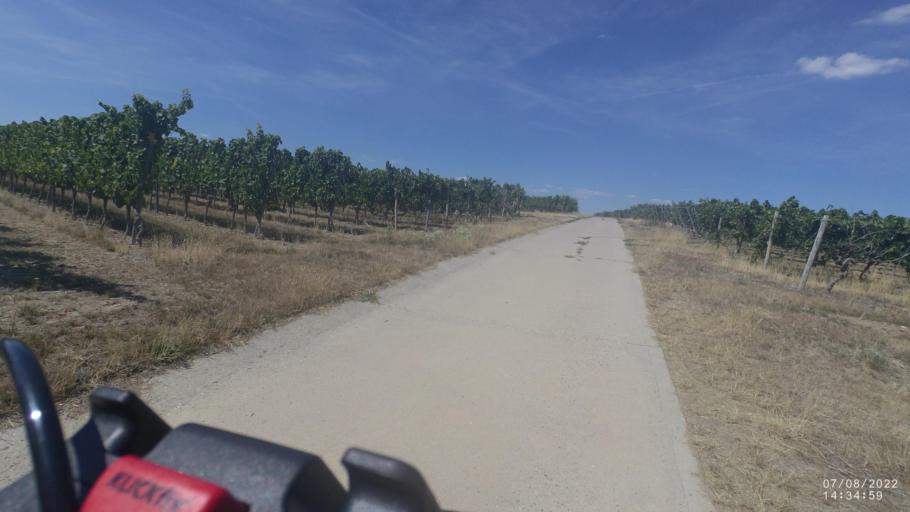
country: DE
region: Rheinland-Pfalz
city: Udenheim
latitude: 49.8595
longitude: 8.1834
